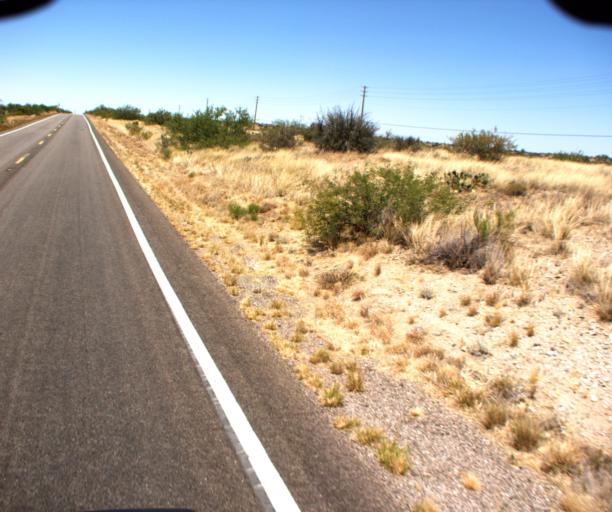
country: US
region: Arizona
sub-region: Pima County
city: Catalina
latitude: 32.5833
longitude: -110.9565
